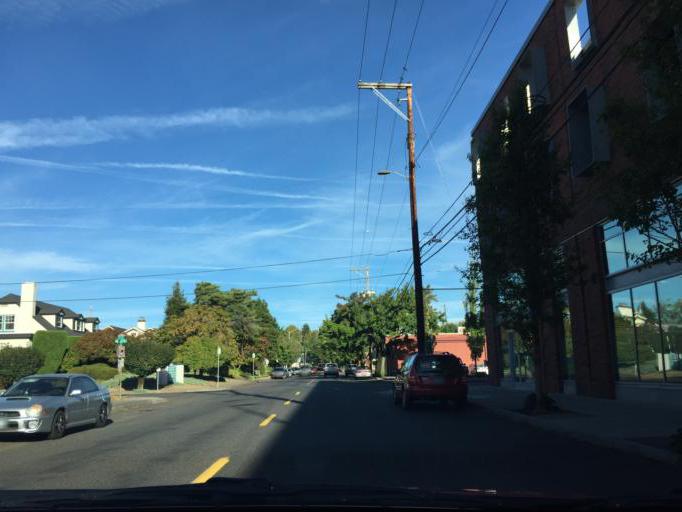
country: US
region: Oregon
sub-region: Multnomah County
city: Portland
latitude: 45.5378
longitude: -122.6185
